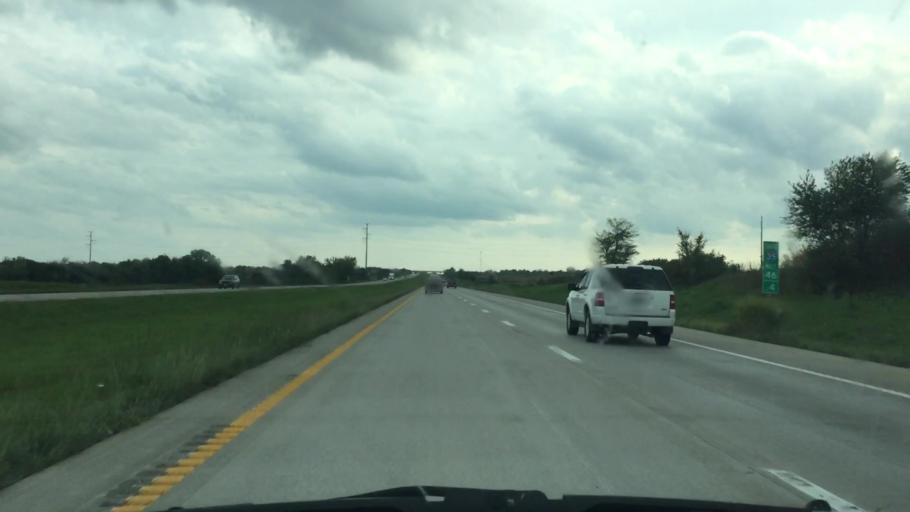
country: US
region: Missouri
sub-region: Clinton County
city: Cameron
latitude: 39.6420
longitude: -94.2422
